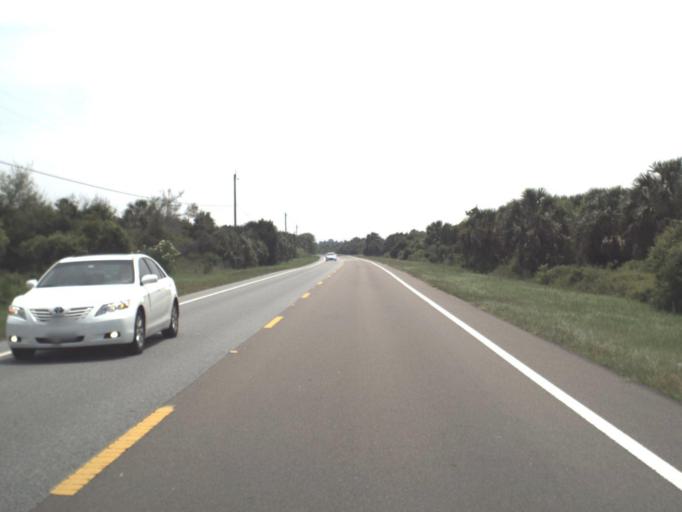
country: US
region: Florida
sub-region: Duval County
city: Atlantic Beach
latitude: 30.4487
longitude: -81.4157
